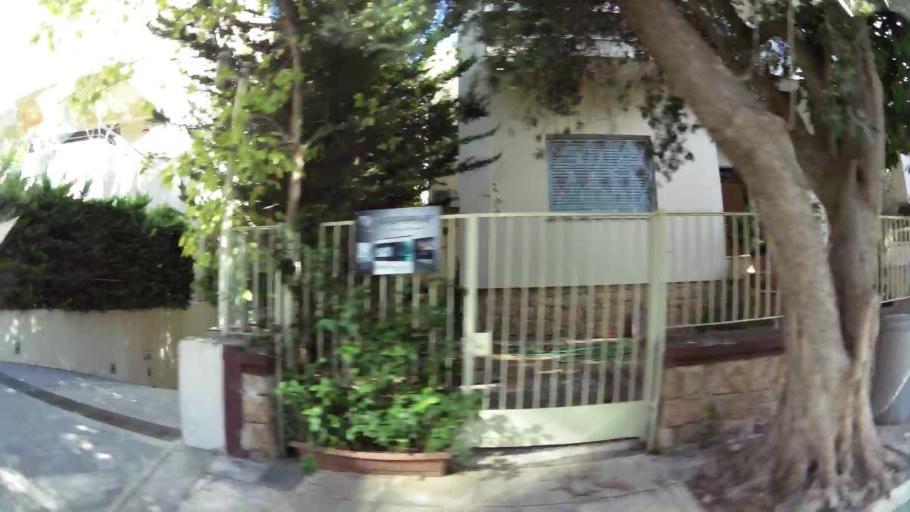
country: GR
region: Attica
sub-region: Nomarchia Athinas
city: Neo Psychiko
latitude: 38.0023
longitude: 23.7788
